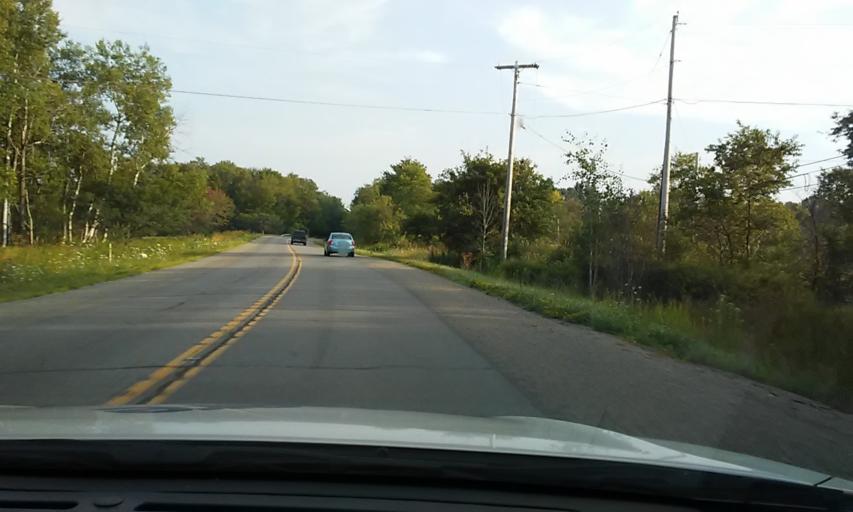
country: US
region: Pennsylvania
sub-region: McKean County
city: Kane
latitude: 41.6926
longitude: -78.7189
